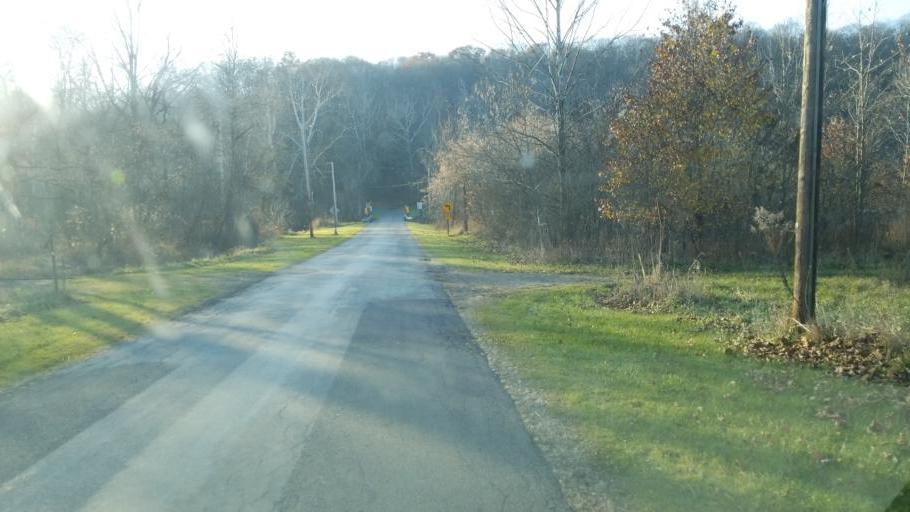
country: US
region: Ohio
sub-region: Wayne County
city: Wooster
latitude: 40.8950
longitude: -82.0095
